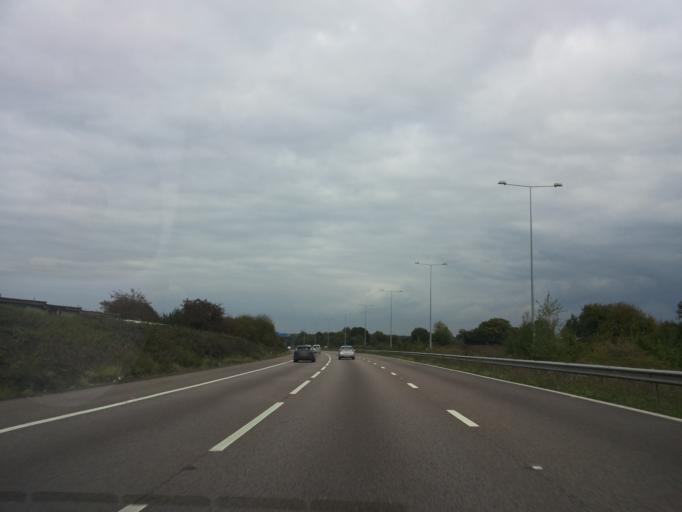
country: GB
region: England
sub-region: Kent
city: Boxley
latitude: 51.3264
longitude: 0.5617
